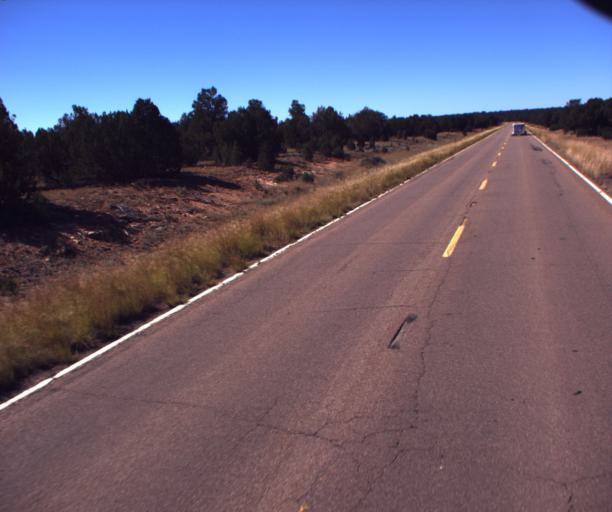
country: US
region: Arizona
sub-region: Navajo County
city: Heber-Overgaard
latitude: 34.4588
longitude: -110.5124
